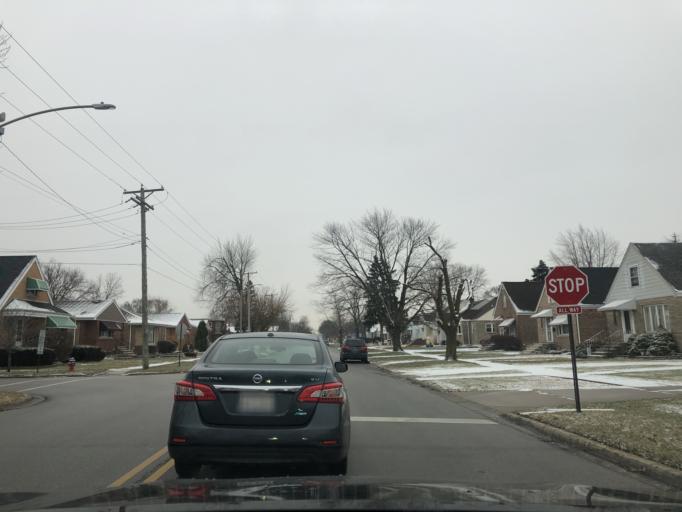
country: US
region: Illinois
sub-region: Cook County
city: Evergreen Park
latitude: 41.7339
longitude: -87.6923
